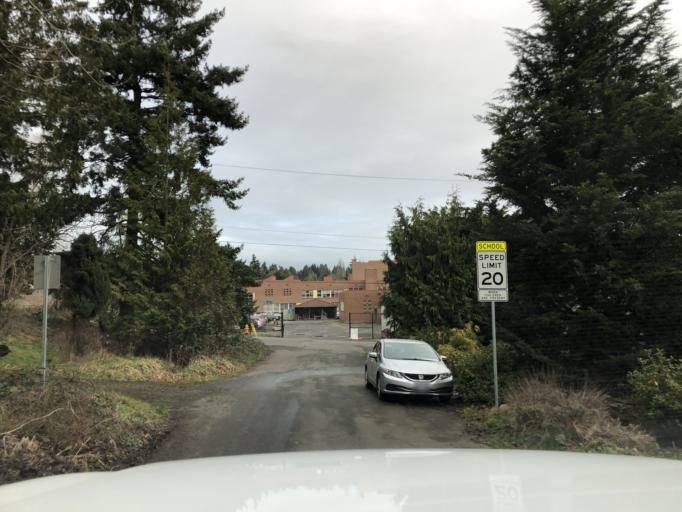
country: US
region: Washington
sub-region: King County
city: Lake Forest Park
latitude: 47.7102
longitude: -122.2955
